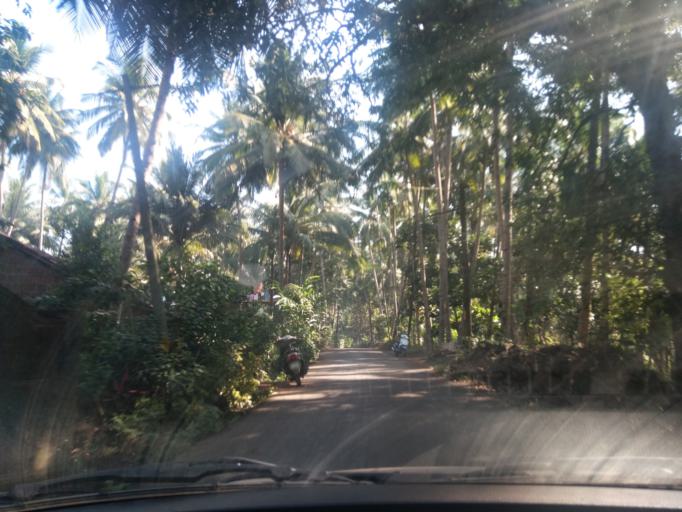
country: IN
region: Goa
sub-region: South Goa
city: Quepem
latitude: 15.1665
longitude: 74.1027
